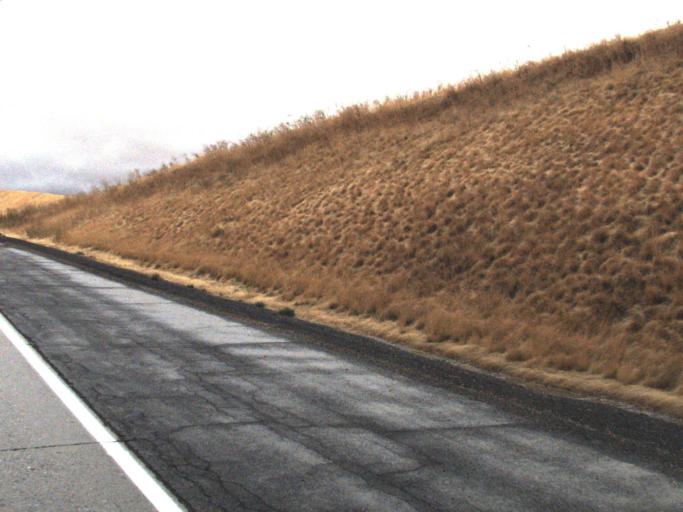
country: US
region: Washington
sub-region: Whitman County
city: Colfax
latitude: 47.0915
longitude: -117.3797
